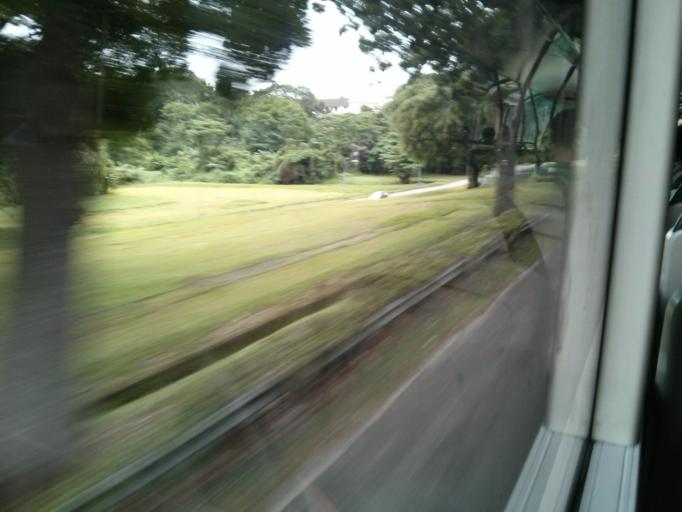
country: SG
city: Singapore
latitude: 1.2865
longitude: 103.7973
